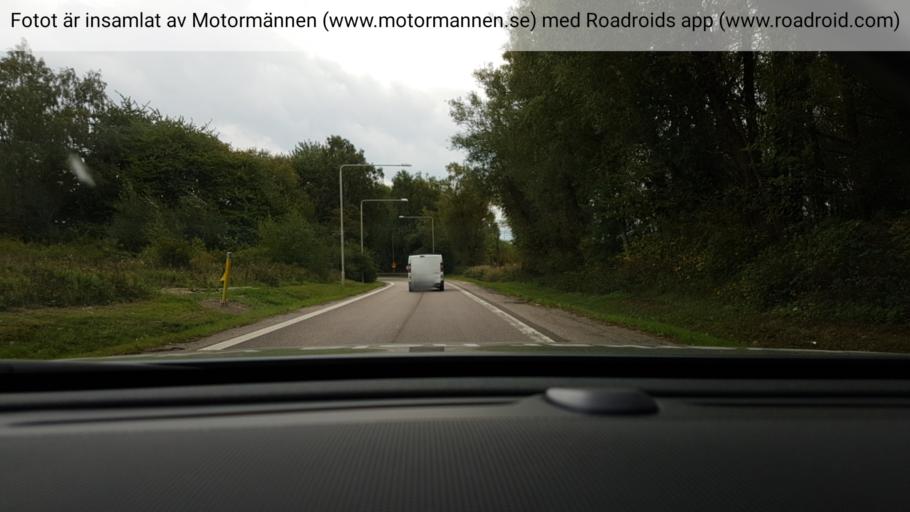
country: SE
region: Vaestra Goetaland
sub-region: Goteborg
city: Goeteborg
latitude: 57.7258
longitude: 11.9687
